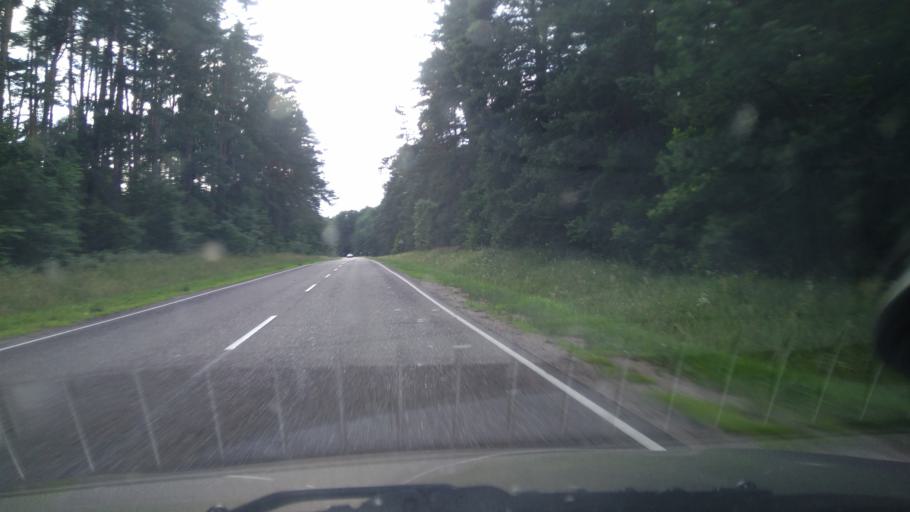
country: BY
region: Grodnenskaya
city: Masty
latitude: 53.3473
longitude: 24.6568
